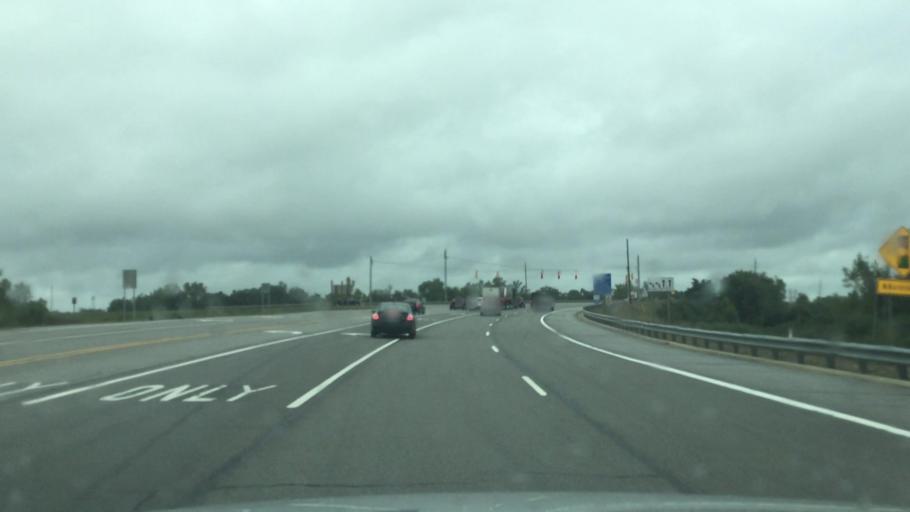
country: US
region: Michigan
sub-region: Livingston County
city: Howell
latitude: 42.6173
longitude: -83.9906
